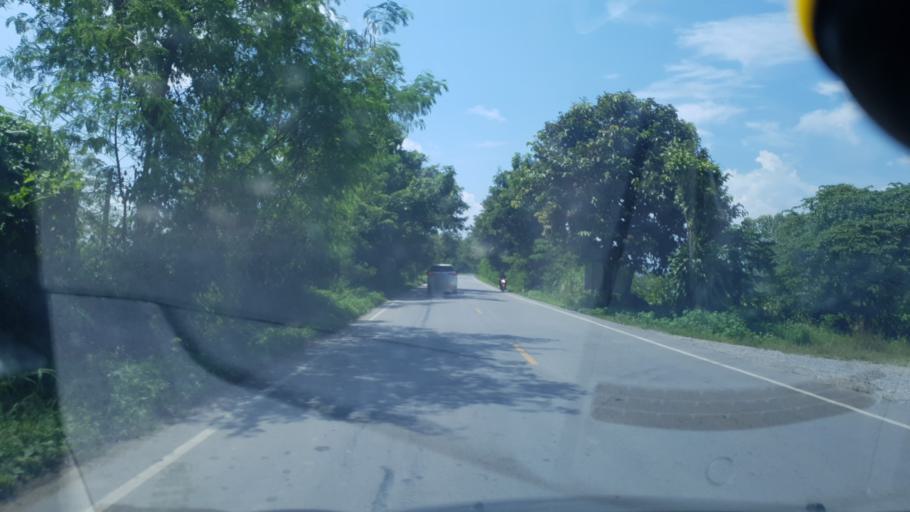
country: TH
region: Chiang Rai
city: Wiang Chai
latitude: 19.9636
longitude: 99.9604
